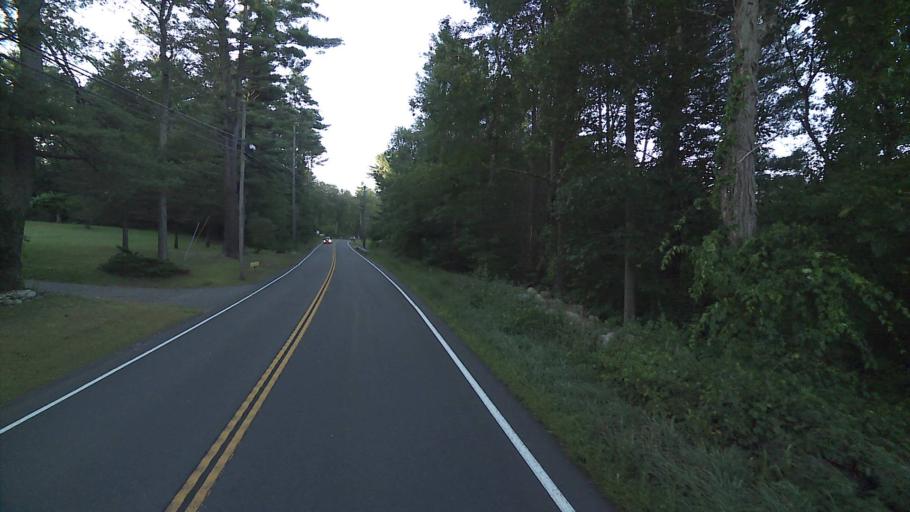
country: US
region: Connecticut
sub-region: Tolland County
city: Stafford
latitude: 41.9866
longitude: -72.3173
